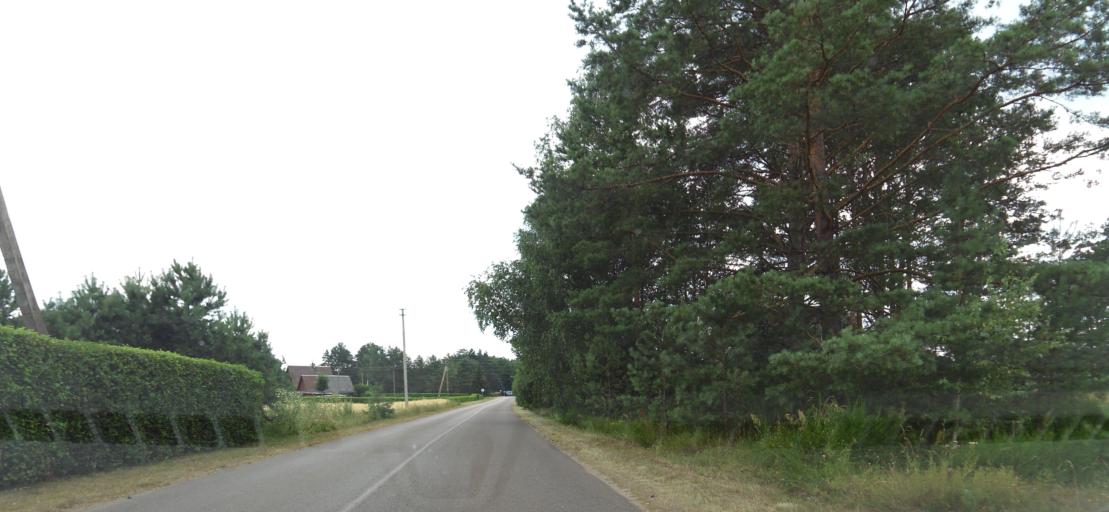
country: LT
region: Alytaus apskritis
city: Druskininkai
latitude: 53.9912
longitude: 24.0430
